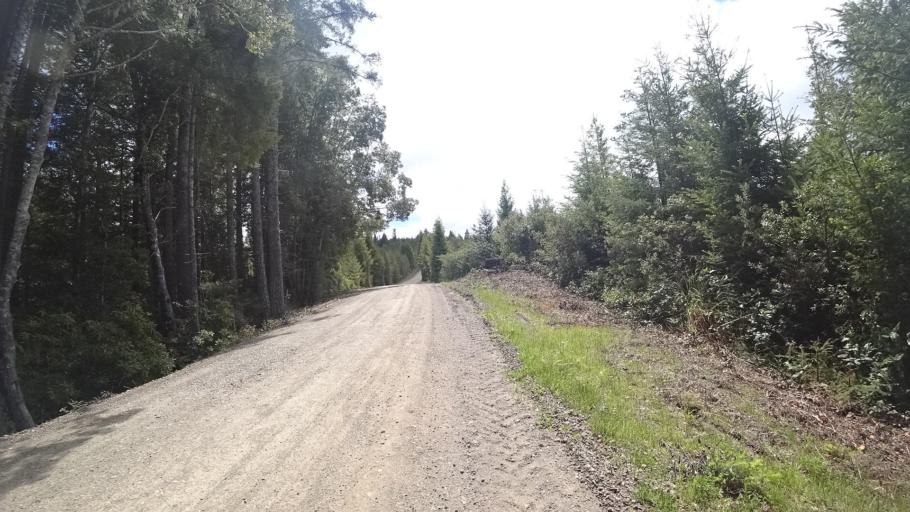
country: US
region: California
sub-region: Humboldt County
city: Blue Lake
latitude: 40.7738
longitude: -123.9636
